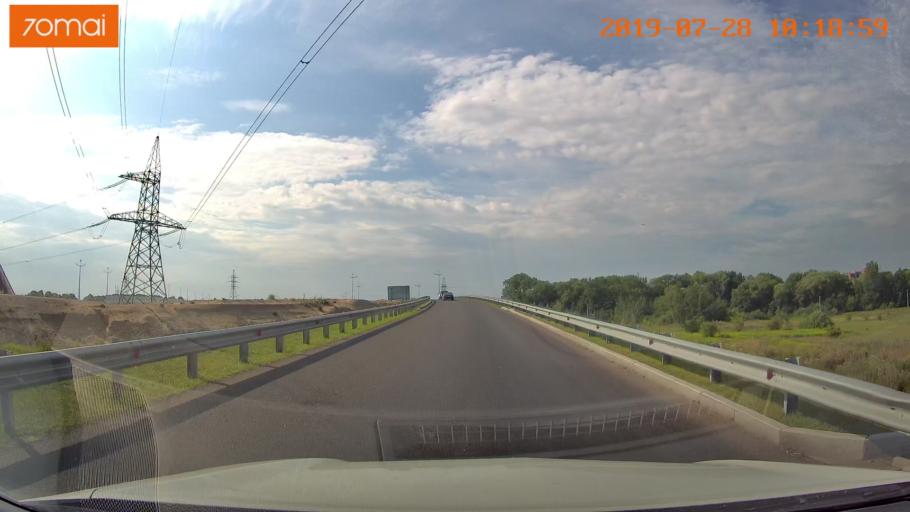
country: RU
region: Kaliningrad
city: Maloye Isakovo
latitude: 54.7518
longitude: 20.5869
